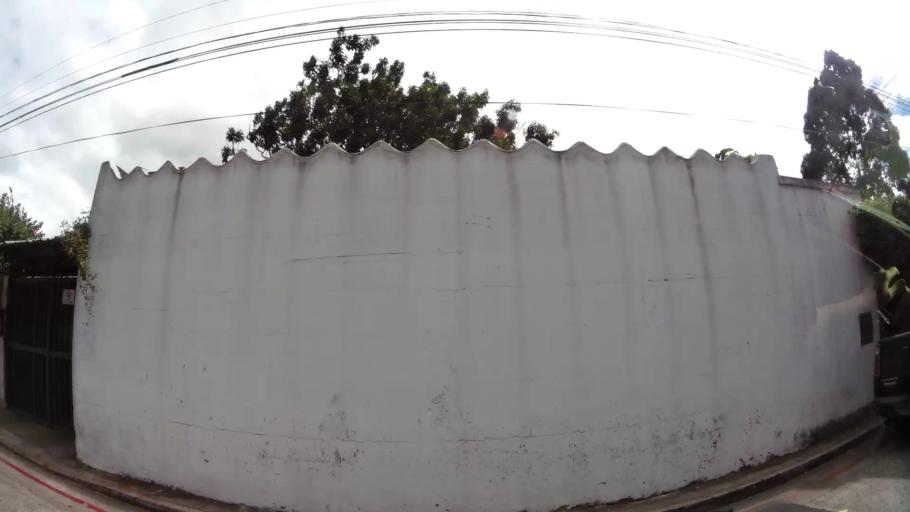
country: GT
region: Guatemala
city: Guatemala City
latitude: 14.6074
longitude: -90.5143
